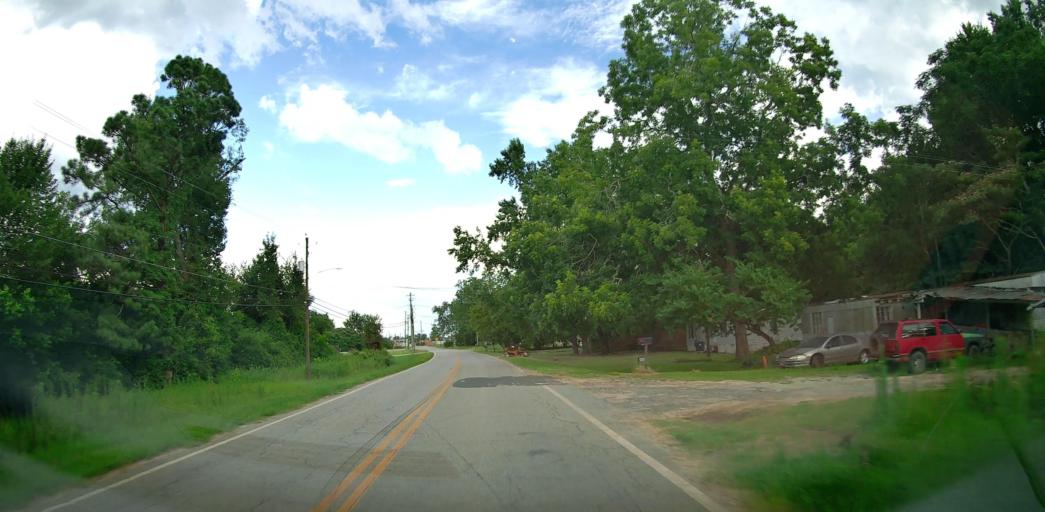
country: US
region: Georgia
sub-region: Bleckley County
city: Cochran
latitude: 32.3929
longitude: -83.3625
